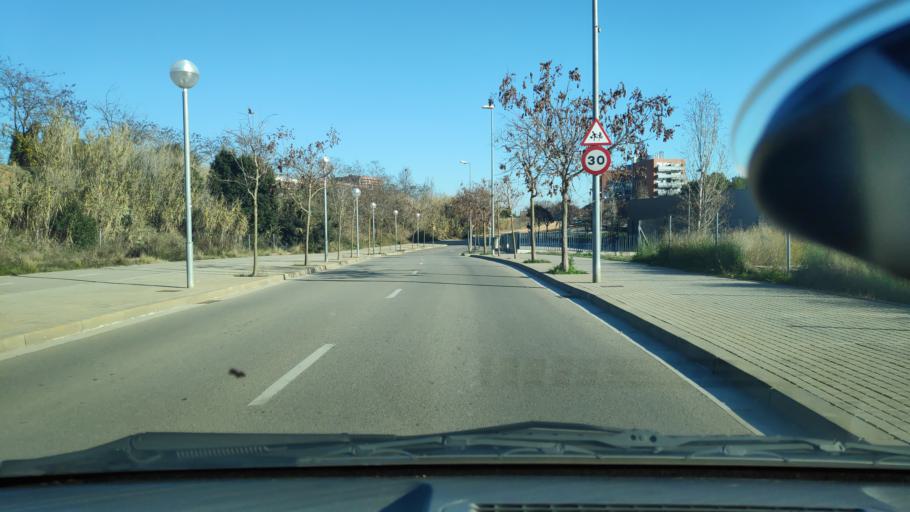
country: ES
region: Catalonia
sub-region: Provincia de Barcelona
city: Sant Quirze del Valles
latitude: 41.5634
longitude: 2.0775
